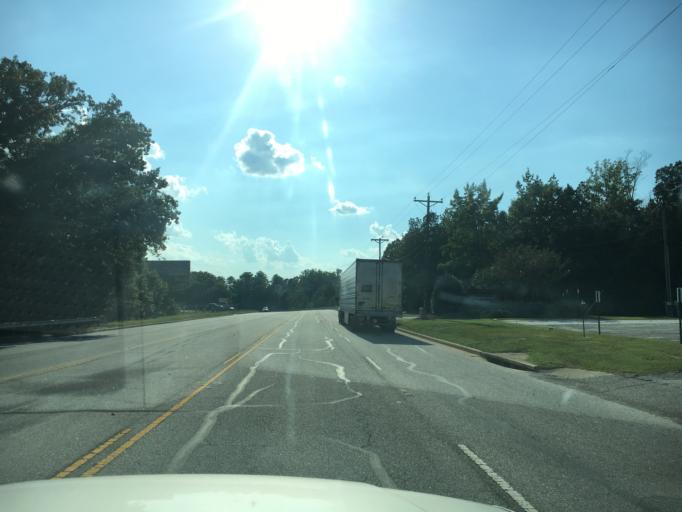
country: US
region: South Carolina
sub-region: Greenwood County
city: Ninety Six
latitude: 34.2869
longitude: -82.0512
